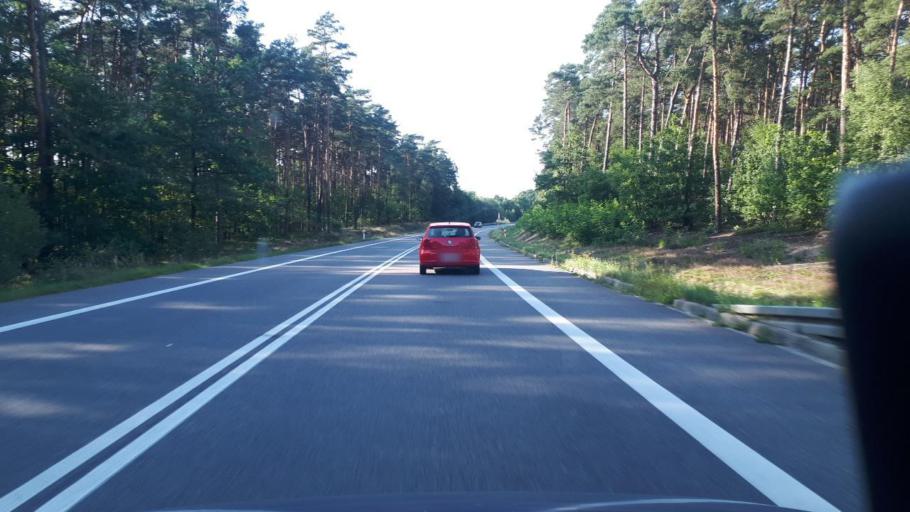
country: PL
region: Silesian Voivodeship
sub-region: Powiat lubliniecki
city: Lubliniec
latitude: 50.6594
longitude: 18.6557
